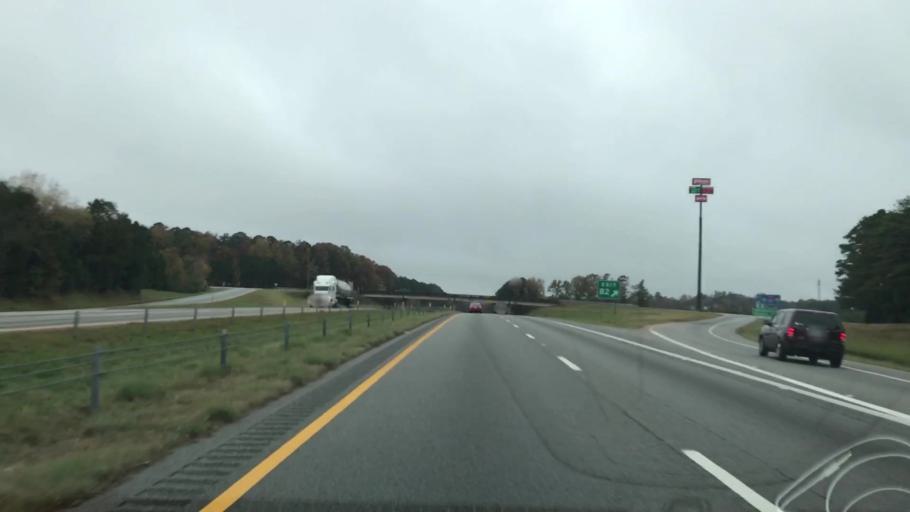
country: US
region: South Carolina
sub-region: Newberry County
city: Prosperity
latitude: 34.2381
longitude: -81.4577
